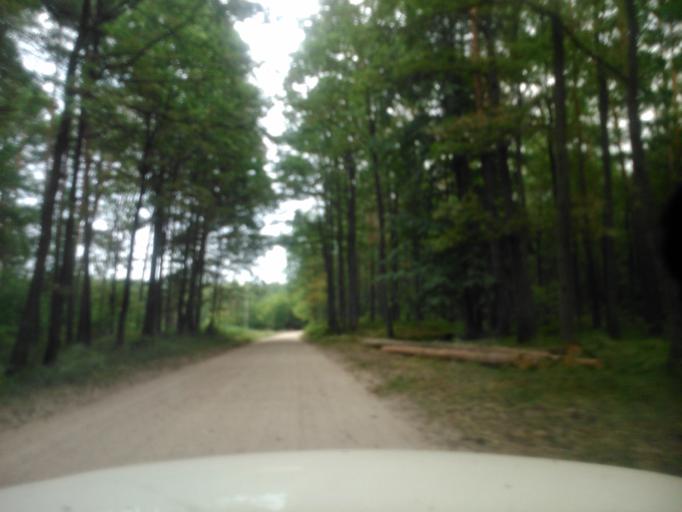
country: PL
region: Kujawsko-Pomorskie
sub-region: Powiat brodnicki
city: Gorzno
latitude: 53.2009
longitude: 19.7036
